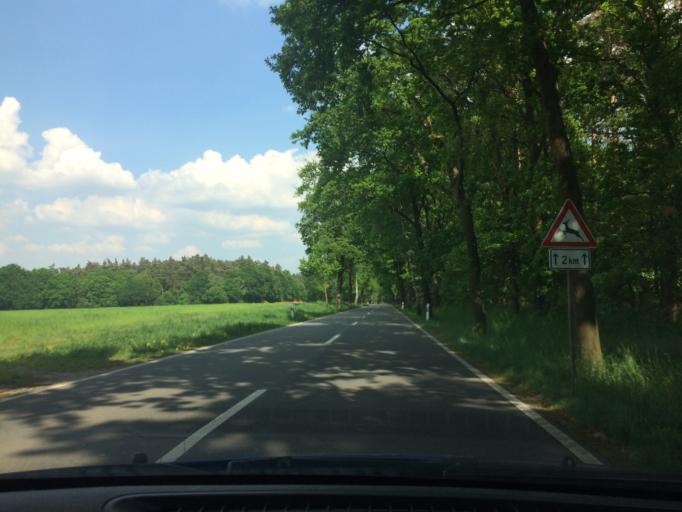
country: DE
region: Lower Saxony
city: Tosterglope
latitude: 53.2155
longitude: 10.8462
